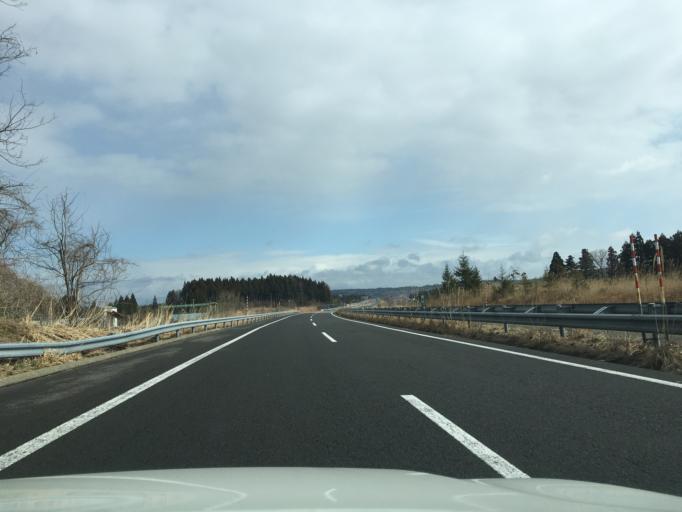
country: JP
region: Akita
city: Akita
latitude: 39.6115
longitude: 140.1398
